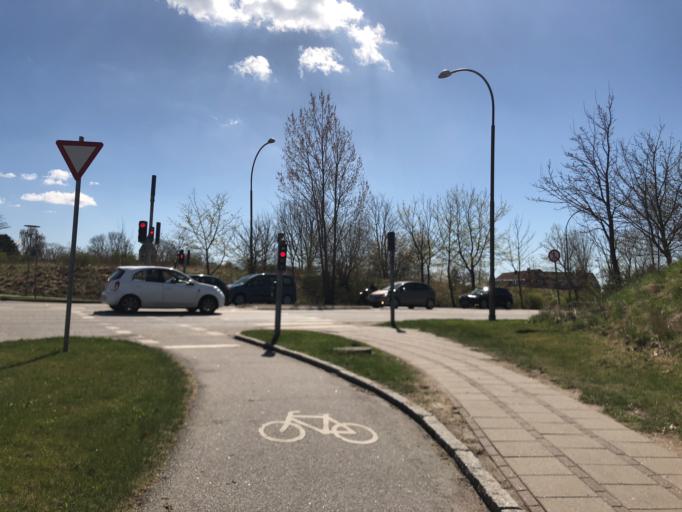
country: DK
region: Zealand
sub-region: Ringsted Kommune
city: Ringsted
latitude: 55.4498
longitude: 11.7838
